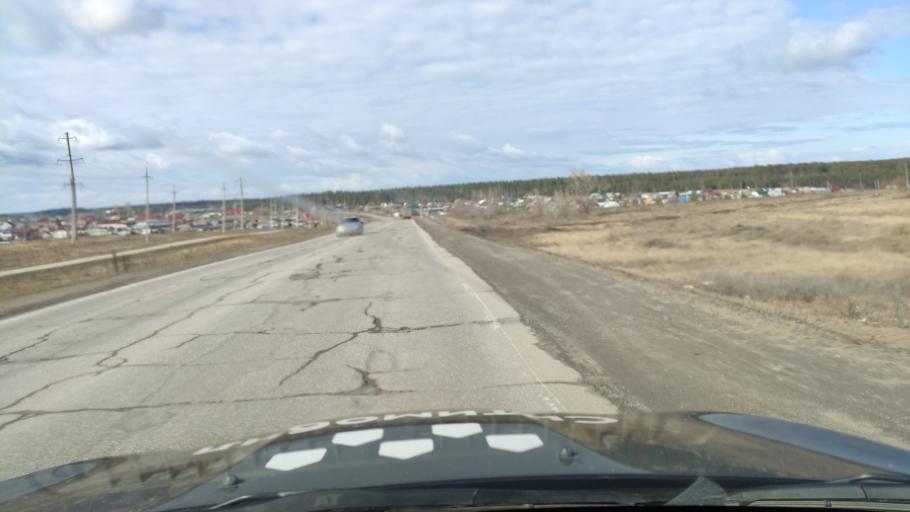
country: RU
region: Samara
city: Povolzhskiy
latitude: 53.5878
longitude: 49.7415
